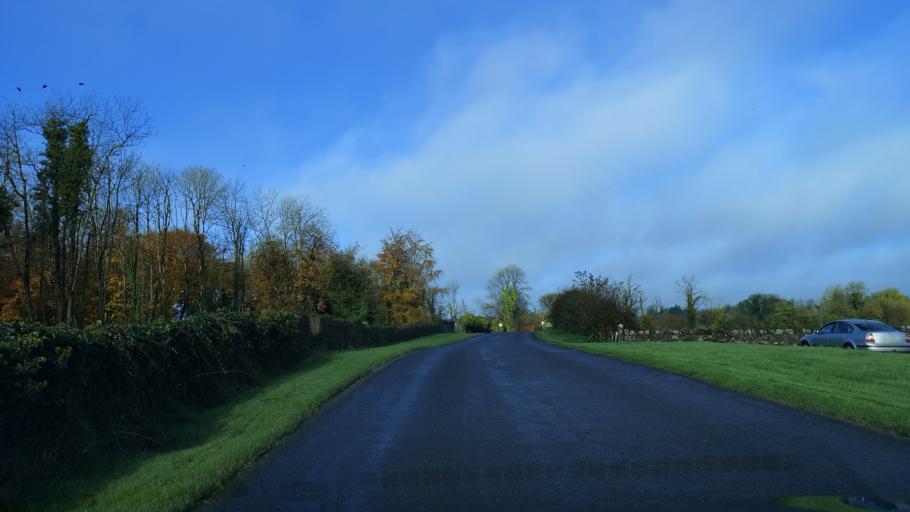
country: IE
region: Leinster
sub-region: An Iarmhi
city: Moate
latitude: 53.3808
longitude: -7.8018
